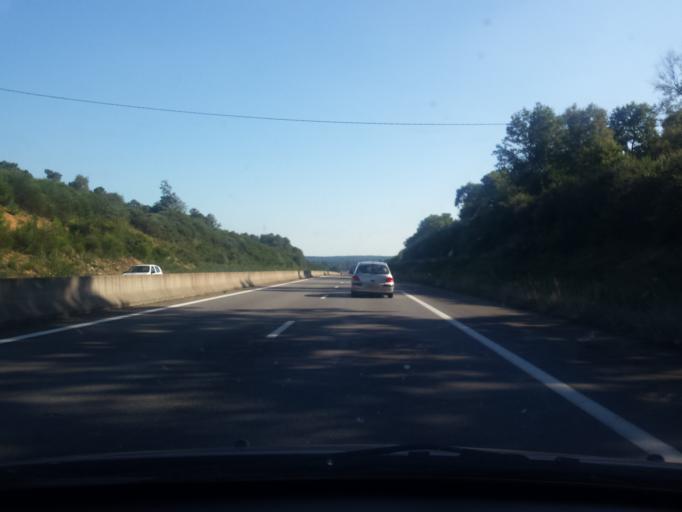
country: FR
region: Brittany
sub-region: Departement du Morbihan
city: Colpo
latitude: 47.7965
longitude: -2.8044
